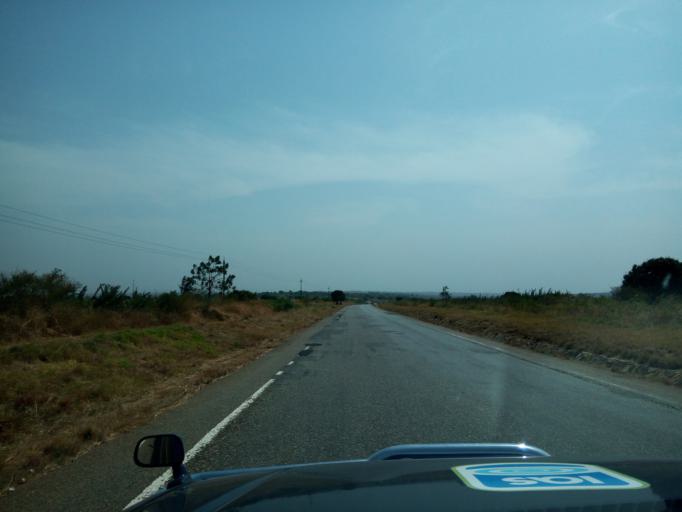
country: UG
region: Northern Region
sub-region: Nebbi District
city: Nebbi
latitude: 2.4638
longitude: 31.2999
